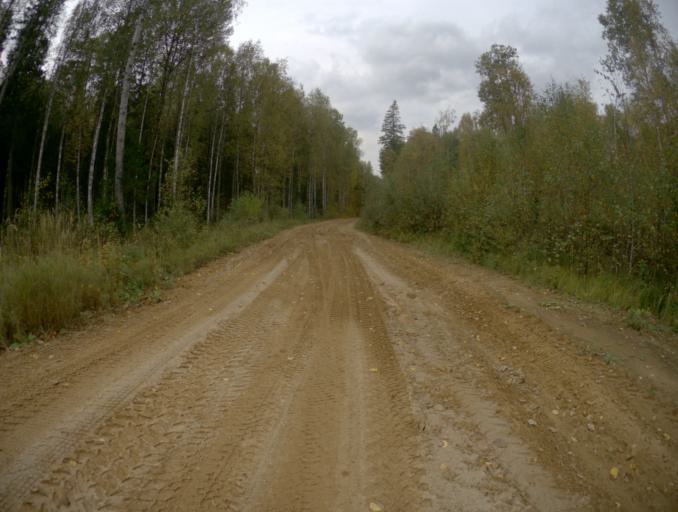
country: RU
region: Vladimir
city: Kideksha
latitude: 56.5004
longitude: 40.7805
